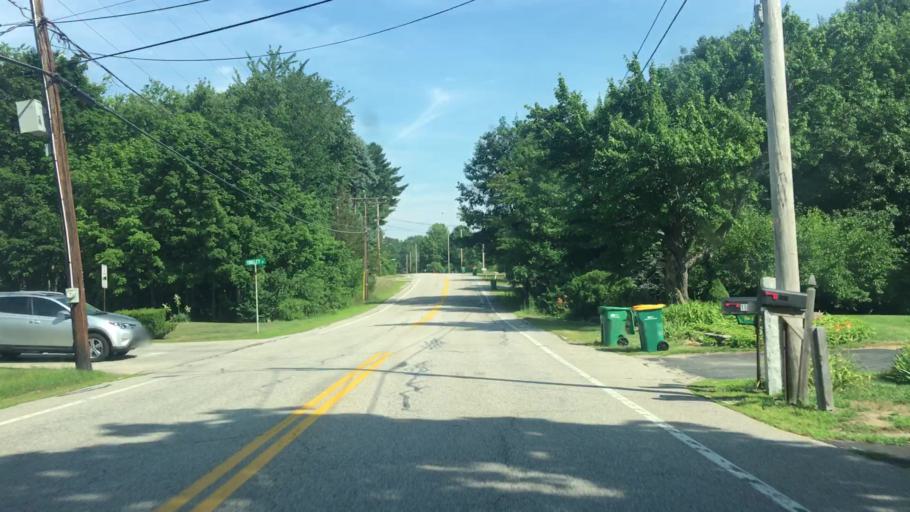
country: US
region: New Hampshire
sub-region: Strafford County
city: Rochester
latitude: 43.2775
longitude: -70.9642
